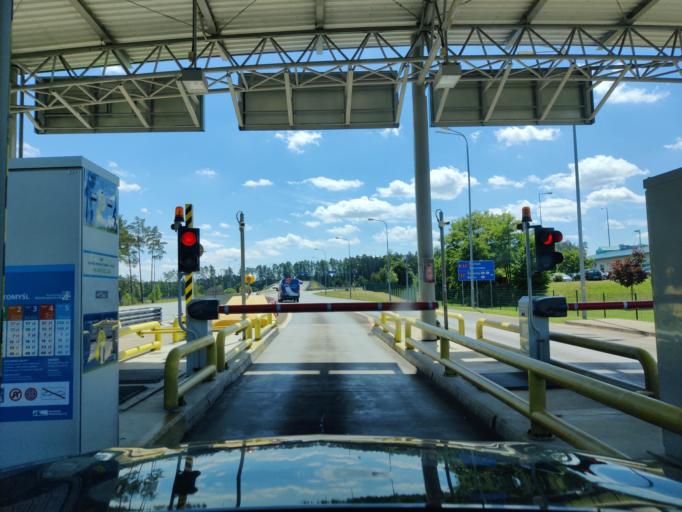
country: PL
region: Greater Poland Voivodeship
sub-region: Powiat nowotomyski
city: Nowy Tomysl
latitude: 52.3616
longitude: 16.0995
